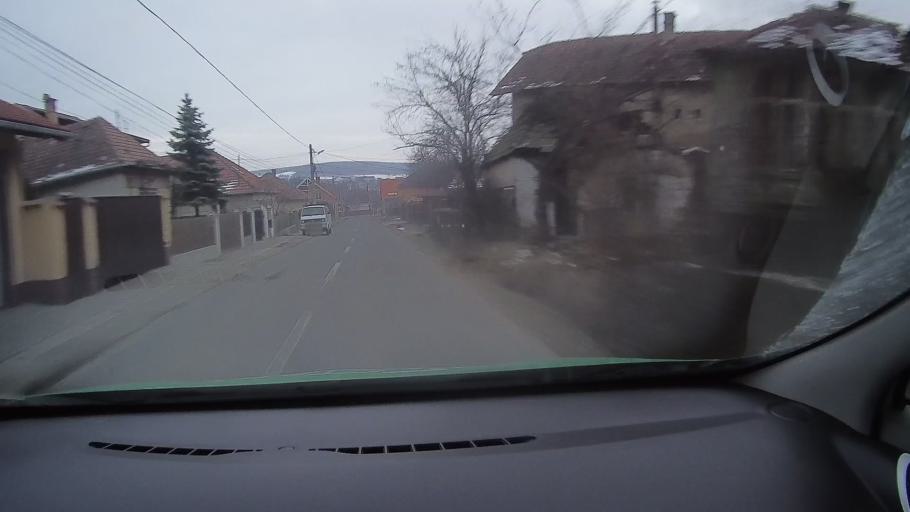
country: RO
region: Harghita
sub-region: Municipiul Odorheiu Secuiesc
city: Odorheiu Secuiesc
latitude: 46.3101
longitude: 25.2852
